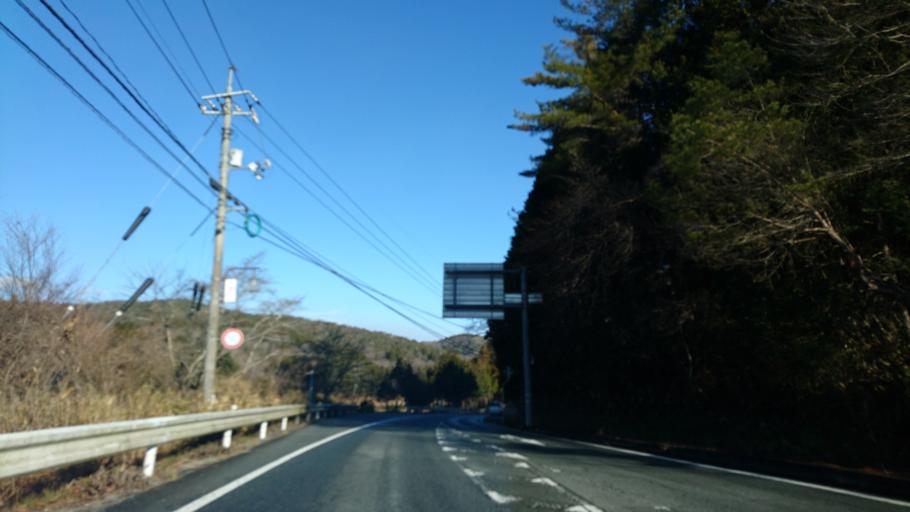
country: JP
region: Okayama
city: Takahashi
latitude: 34.8066
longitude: 133.6724
